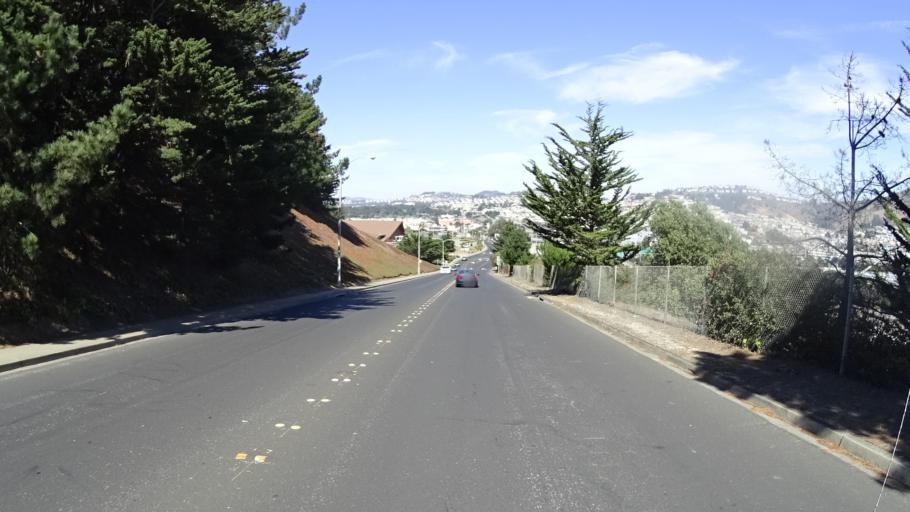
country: US
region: California
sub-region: San Mateo County
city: Broadmoor
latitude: 37.6801
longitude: -122.4729
